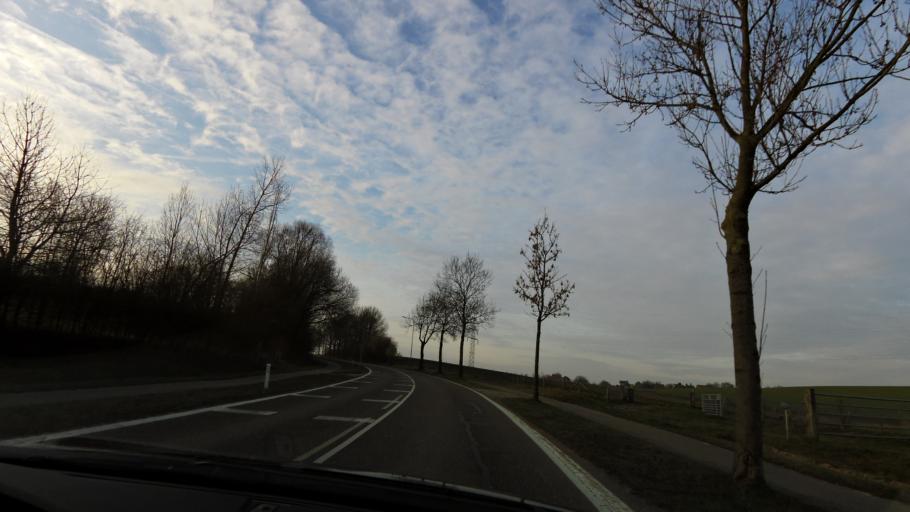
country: NL
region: Limburg
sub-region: Gemeente Beek
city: Beek
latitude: 50.9256
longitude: 5.8366
